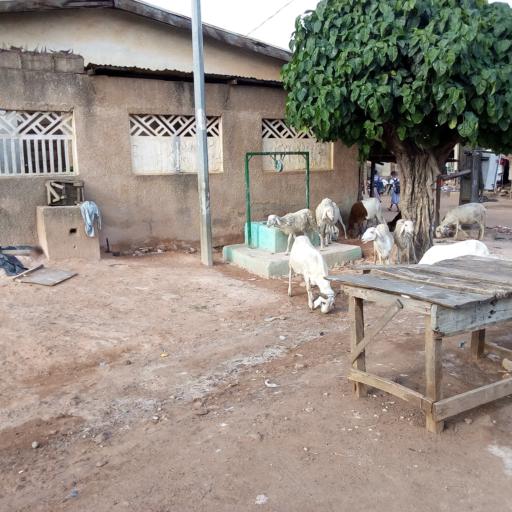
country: CI
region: Vallee du Bandama
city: Bouake
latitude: 7.6910
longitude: -5.0165
